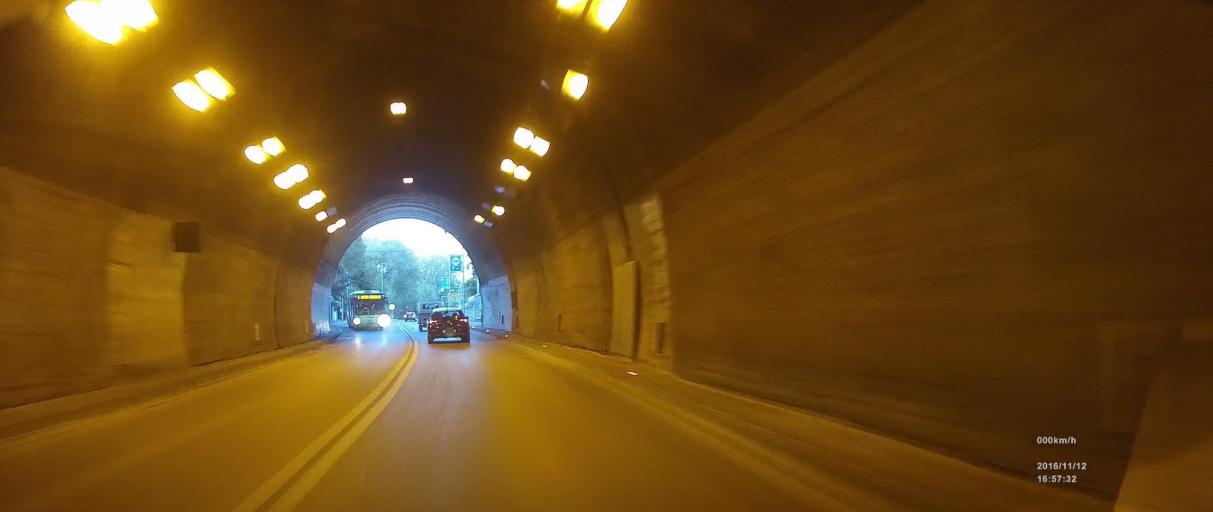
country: HR
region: Splitsko-Dalmatinska
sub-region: Grad Split
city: Split
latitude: 43.5123
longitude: 16.4277
